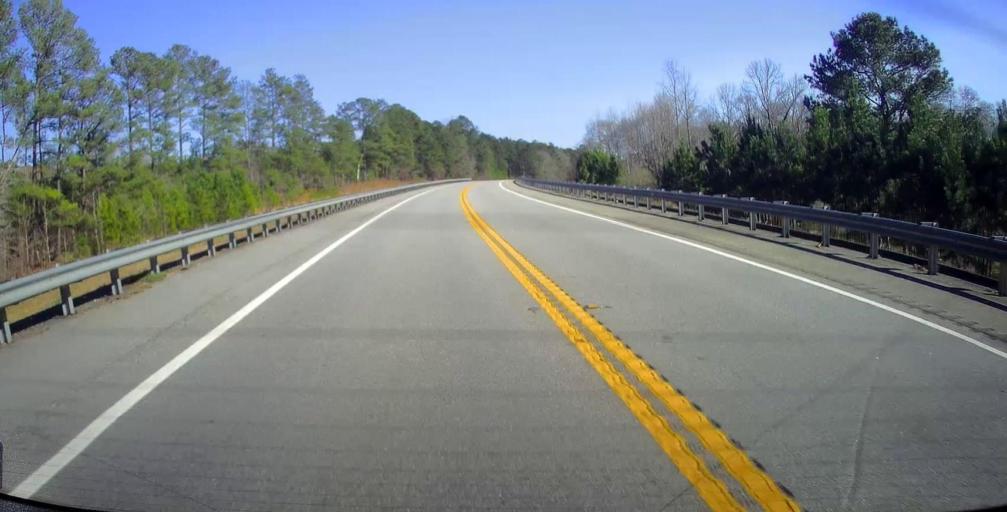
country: US
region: Georgia
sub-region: Macon County
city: Oglethorpe
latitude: 32.3447
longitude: -84.1365
